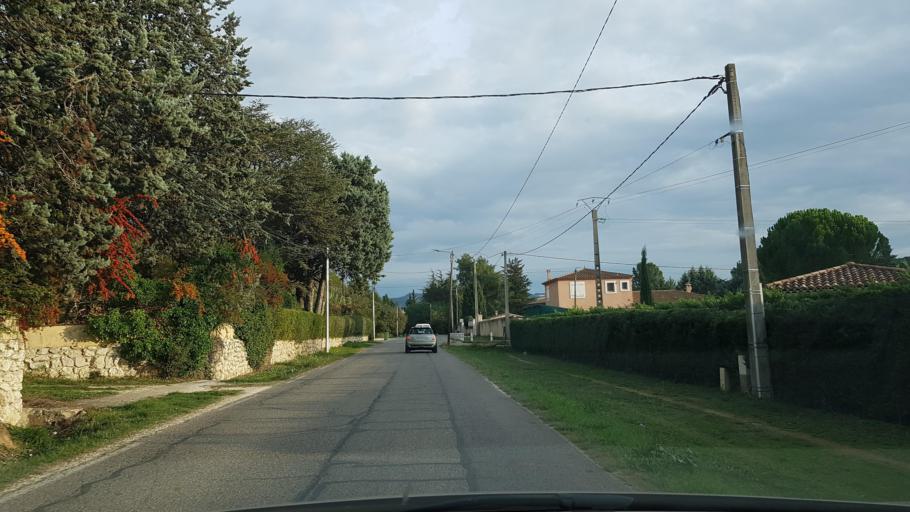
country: FR
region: Provence-Alpes-Cote d'Azur
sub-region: Departement des Bouches-du-Rhone
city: Cabries
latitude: 43.4471
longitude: 5.3686
